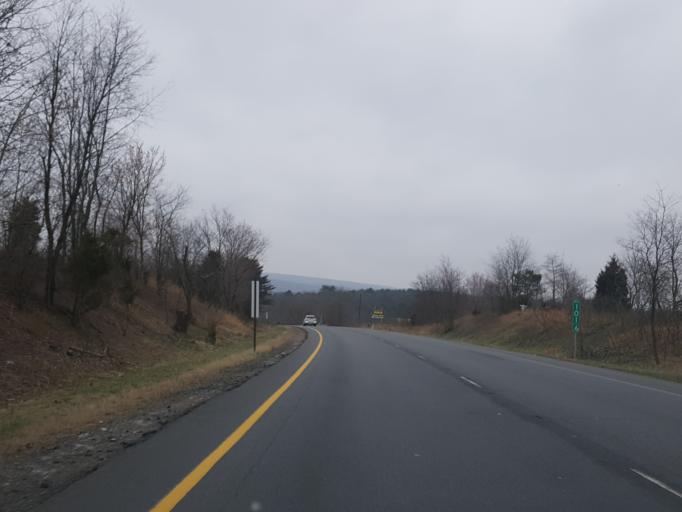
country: US
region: Pennsylvania
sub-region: Schuylkill County
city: Pine Grove
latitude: 40.5630
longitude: -76.4311
